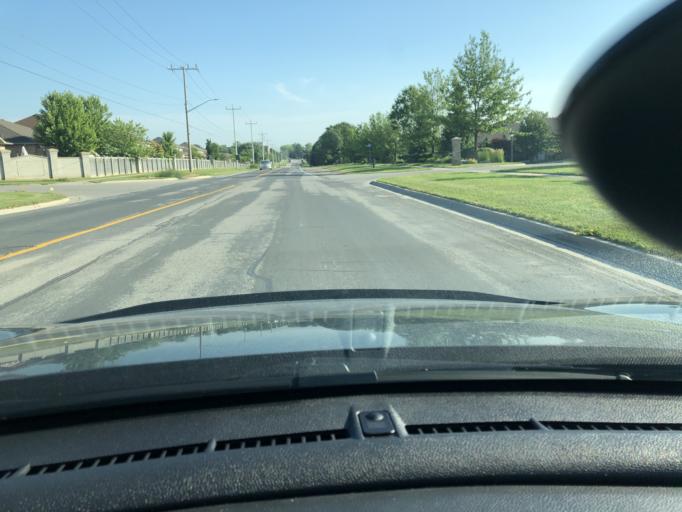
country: CA
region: Ontario
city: Stratford
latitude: 43.3837
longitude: -80.9631
